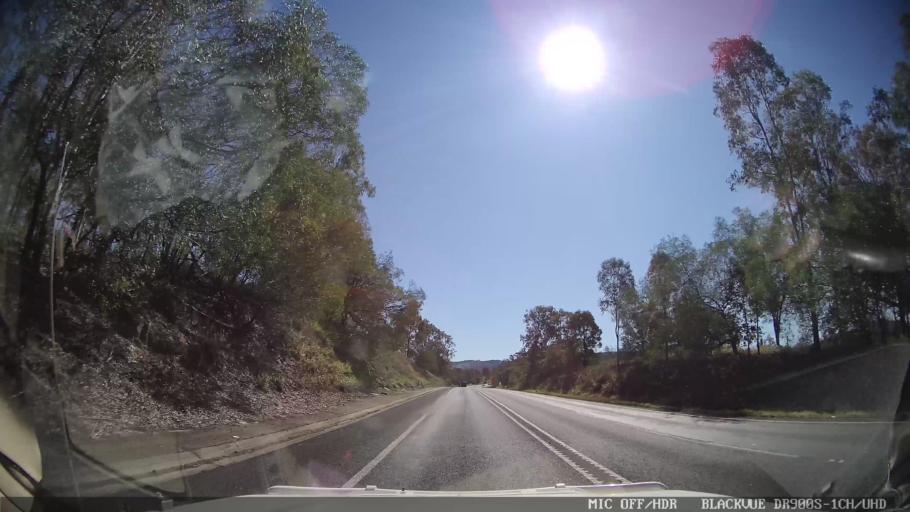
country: AU
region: Queensland
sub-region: Gympie Regional Council
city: Gympie
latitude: -25.9997
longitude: 152.5664
